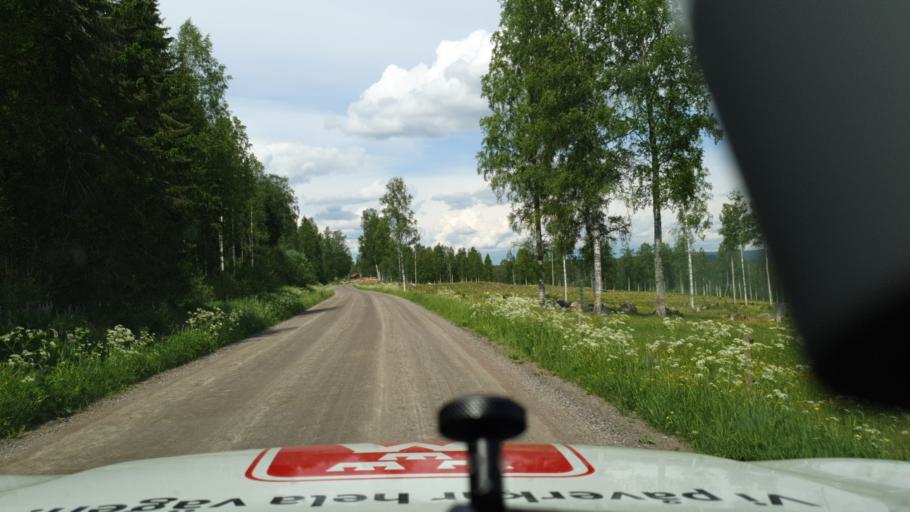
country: SE
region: Vaermland
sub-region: Torsby Kommun
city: Torsby
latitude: 59.9507
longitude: 12.8953
